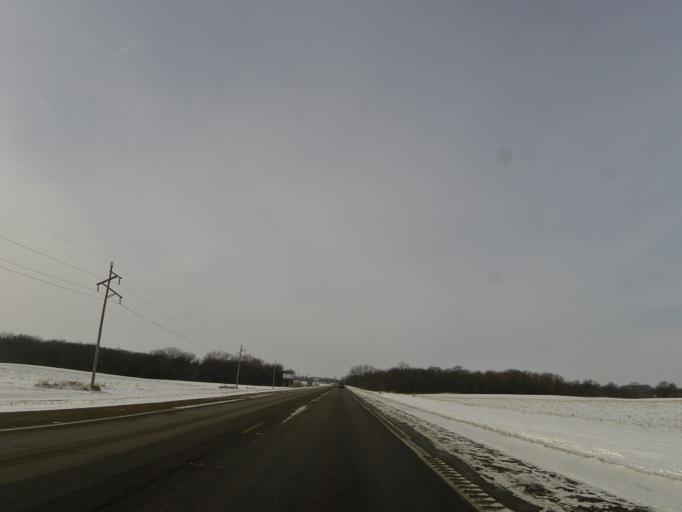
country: US
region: Minnesota
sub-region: Carver County
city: Mayer
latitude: 44.9057
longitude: -93.8769
